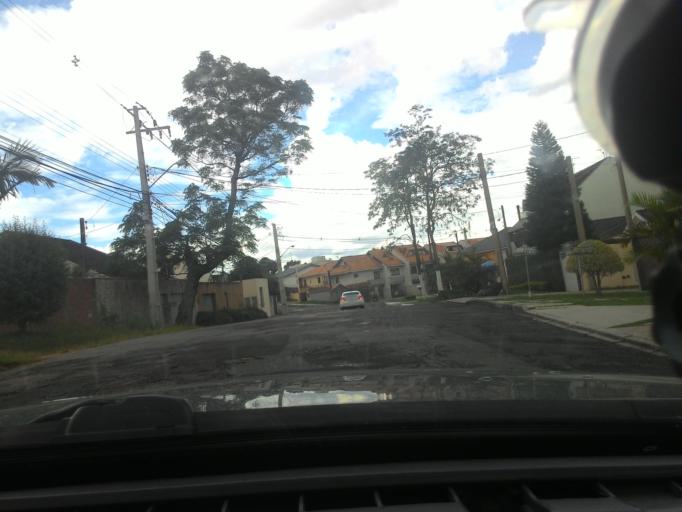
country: BR
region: Parana
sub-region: Pinhais
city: Pinhais
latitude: -25.4627
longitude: -49.2327
